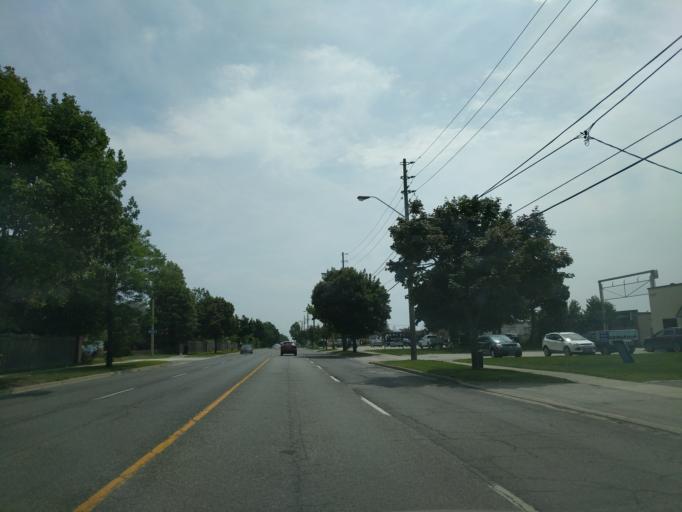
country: CA
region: Ontario
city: Markham
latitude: 43.8248
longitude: -79.2967
